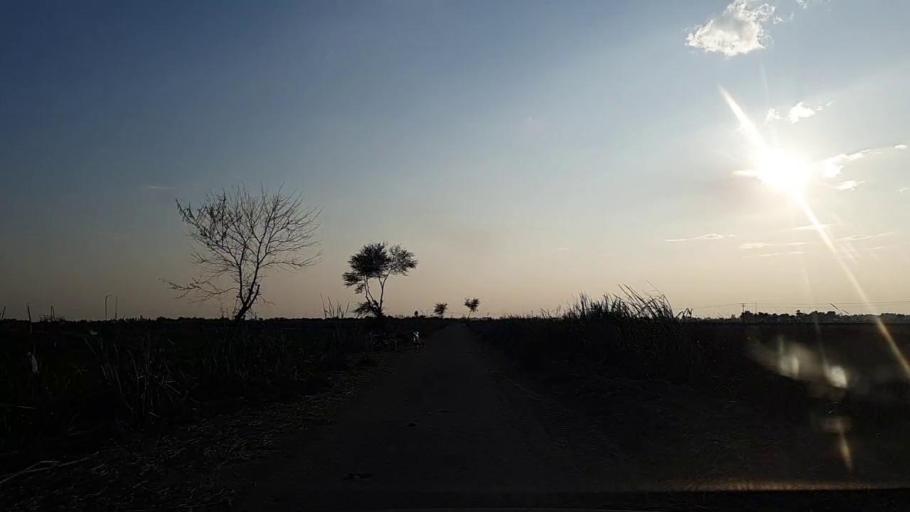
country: PK
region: Sindh
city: Sanghar
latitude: 26.2618
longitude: 68.9787
